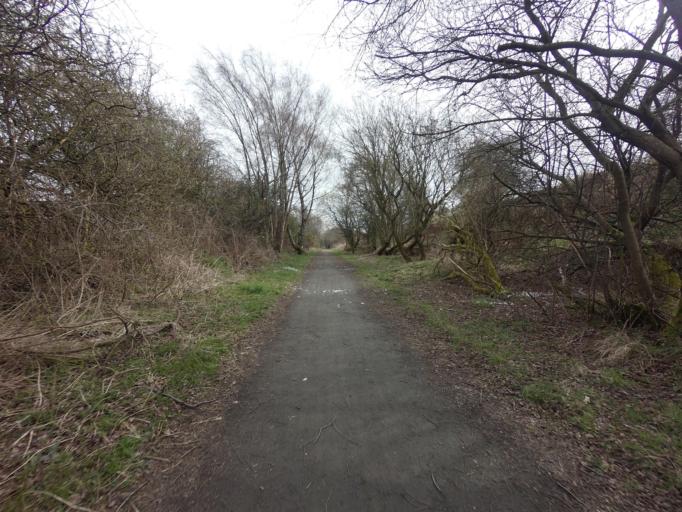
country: GB
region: Scotland
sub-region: West Lothian
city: Broxburn
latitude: 55.9177
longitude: -3.4944
